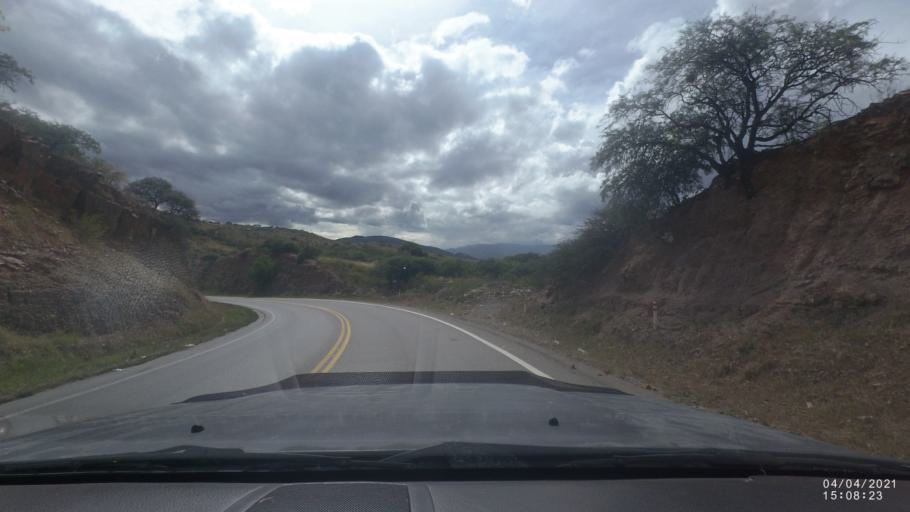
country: BO
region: Cochabamba
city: Capinota
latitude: -17.6018
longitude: -66.3580
